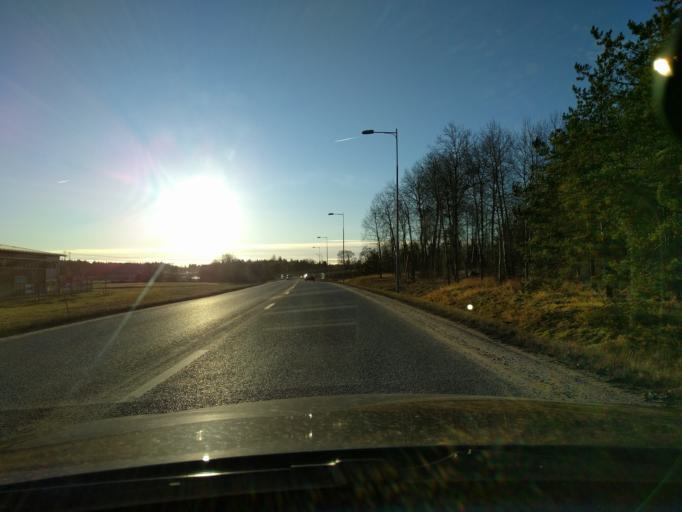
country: SE
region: Stockholm
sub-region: Taby Kommun
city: Taby
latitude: 59.4819
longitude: 18.0544
